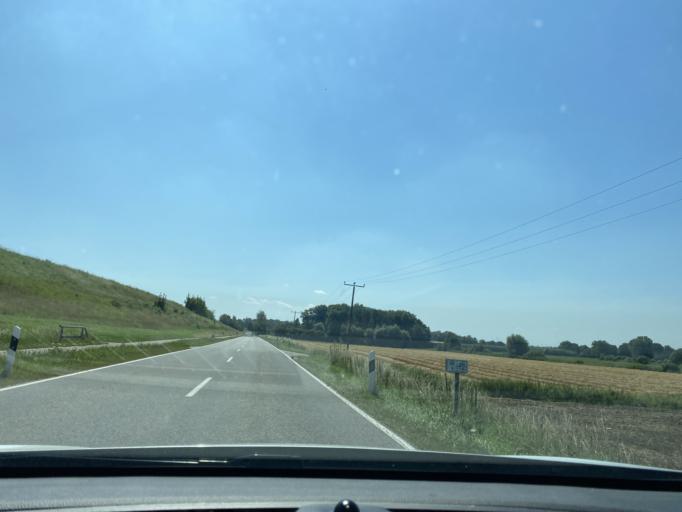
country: DE
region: Bavaria
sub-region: Upper Bavaria
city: Moosinning
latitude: 48.2651
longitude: 11.8454
